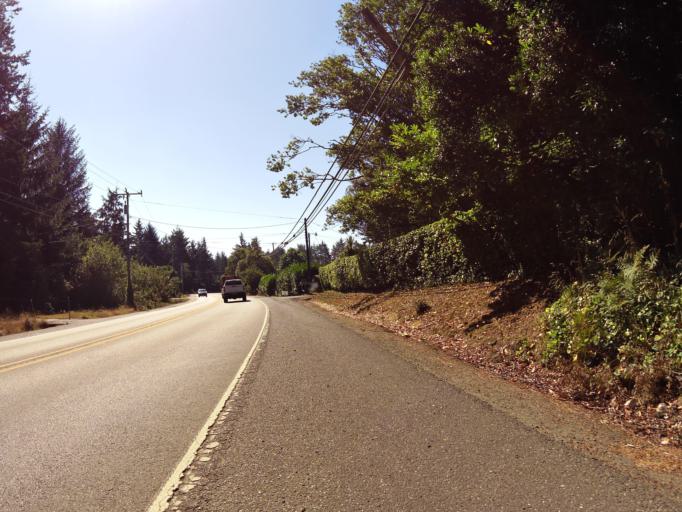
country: US
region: Oregon
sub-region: Coos County
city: Barview
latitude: 43.3520
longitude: -124.3135
